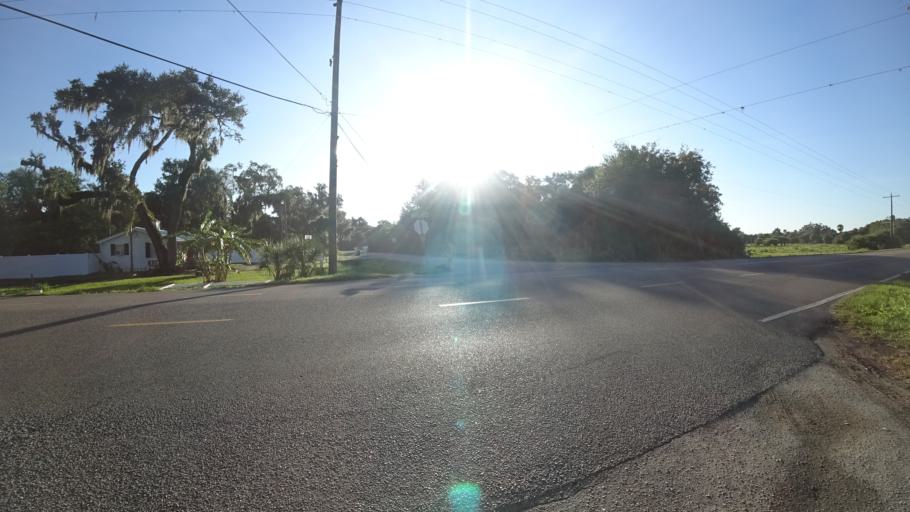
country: US
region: Florida
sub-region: Manatee County
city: Ellenton
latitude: 27.5400
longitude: -82.5284
